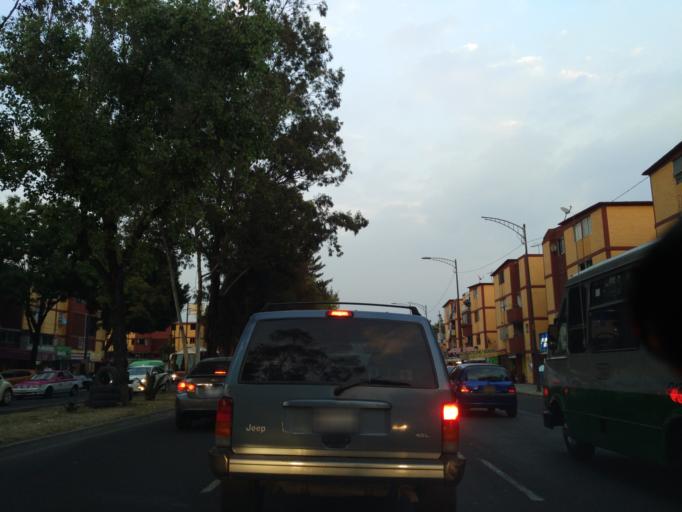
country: MX
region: Mexico City
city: Xochimilco
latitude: 19.3076
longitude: -99.1115
